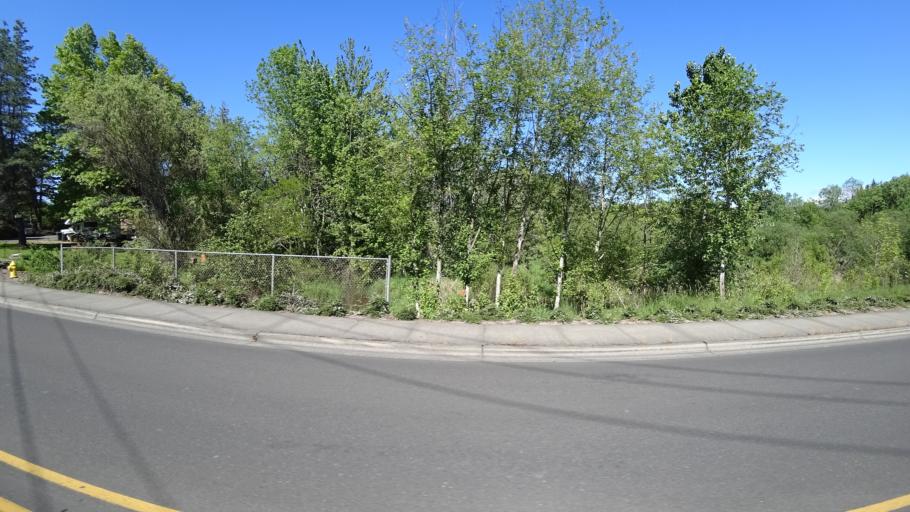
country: US
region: Oregon
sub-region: Washington County
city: Oak Hills
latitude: 45.5470
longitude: -122.8300
